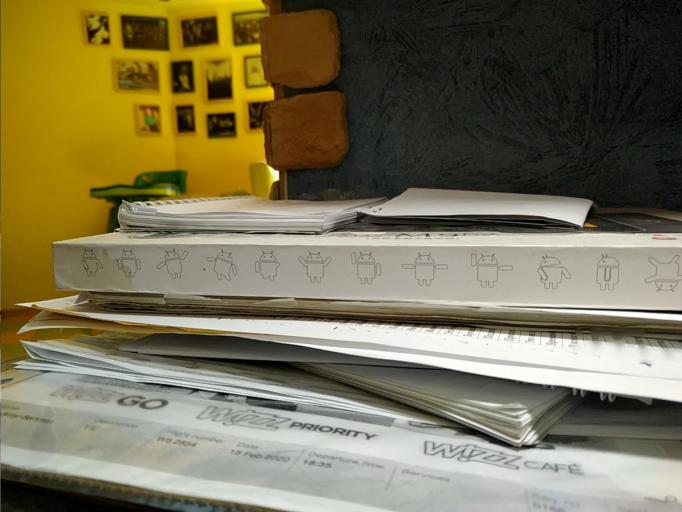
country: RU
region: Novgorod
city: Utorgosh
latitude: 58.1419
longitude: 30.0525
